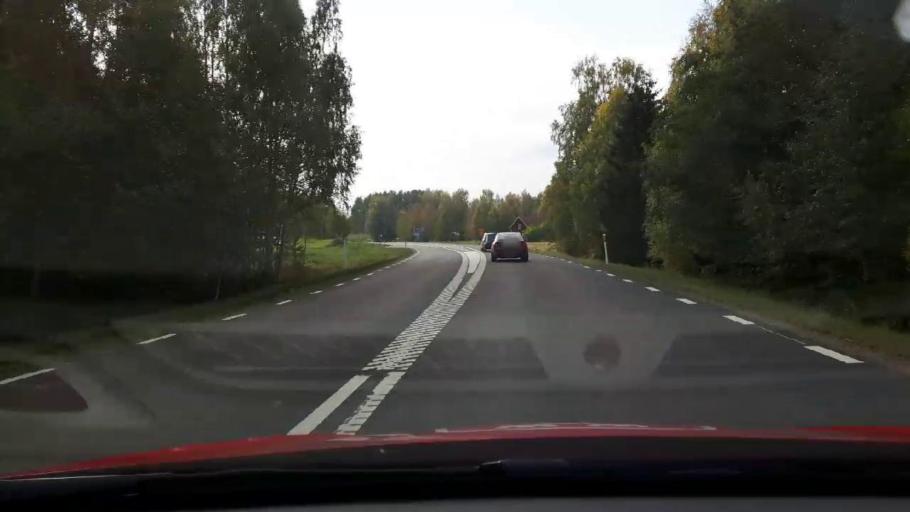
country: SE
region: Gaevleborg
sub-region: Bollnas Kommun
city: Arbra
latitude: 61.4852
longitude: 16.3677
